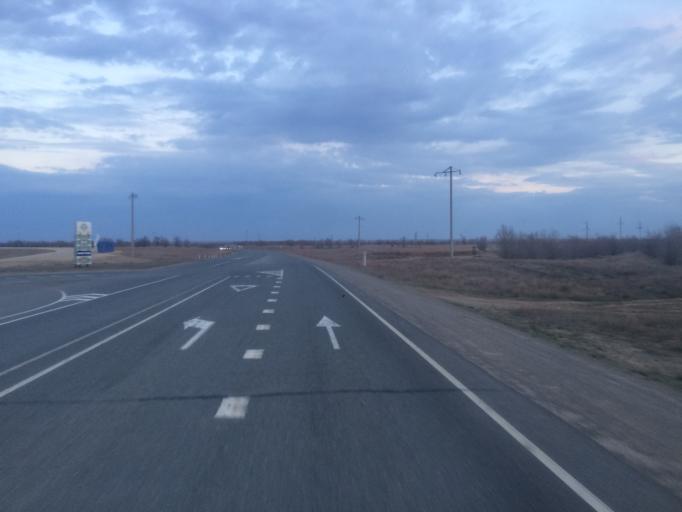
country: KZ
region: Aqtoebe
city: Martuk
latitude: 50.7427
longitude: 56.4703
